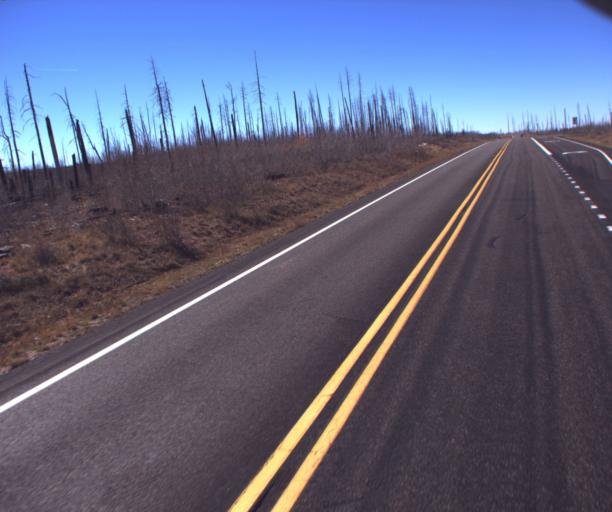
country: US
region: Arizona
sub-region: Coconino County
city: Grand Canyon
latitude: 36.5542
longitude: -112.1750
